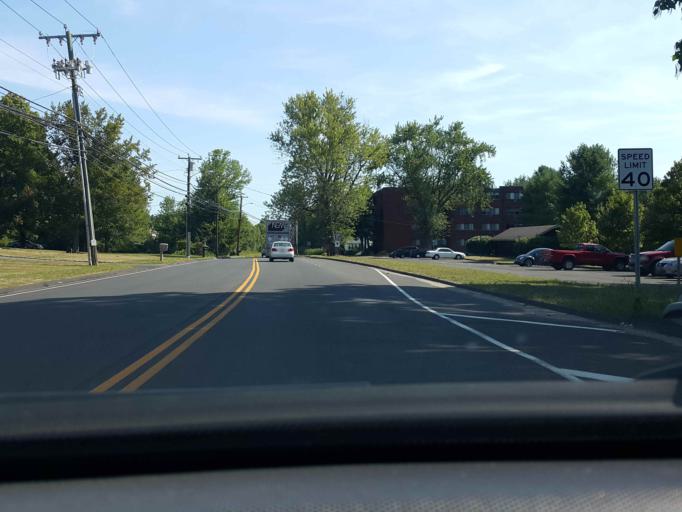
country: US
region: Connecticut
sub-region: Middlesex County
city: Middletown
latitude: 41.5262
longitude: -72.6639
